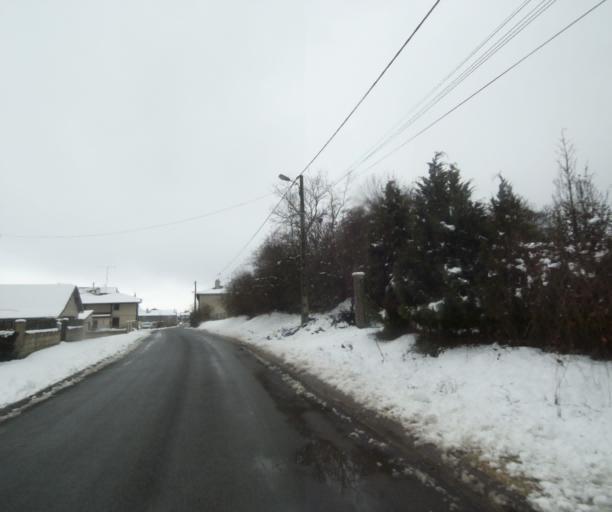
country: FR
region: Champagne-Ardenne
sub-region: Departement de la Haute-Marne
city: Laneuville-a-Remy
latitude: 48.4612
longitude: 4.8516
